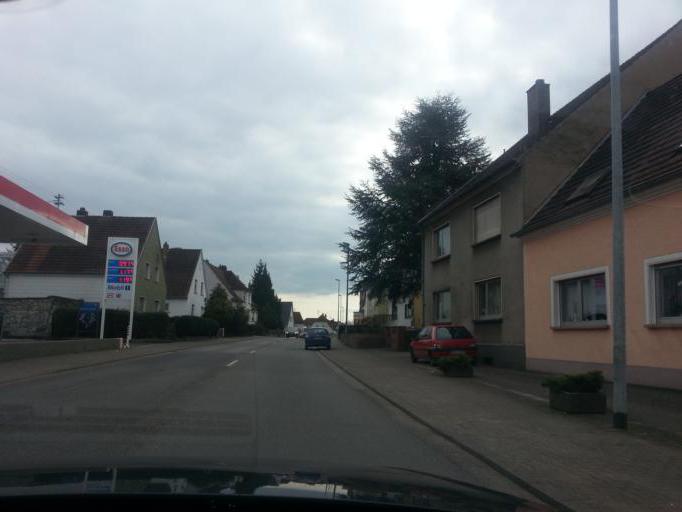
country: DE
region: Saarland
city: Bexbach
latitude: 49.3526
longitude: 7.2662
